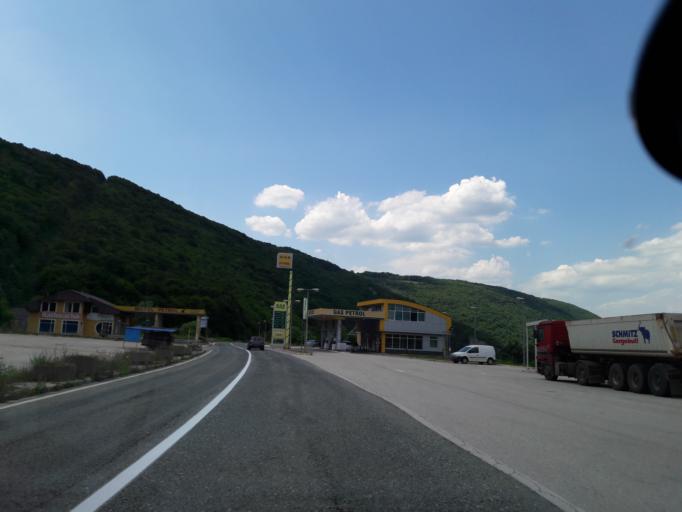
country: BA
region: Republika Srpska
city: Mrkonjic Grad
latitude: 44.4887
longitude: 17.1603
